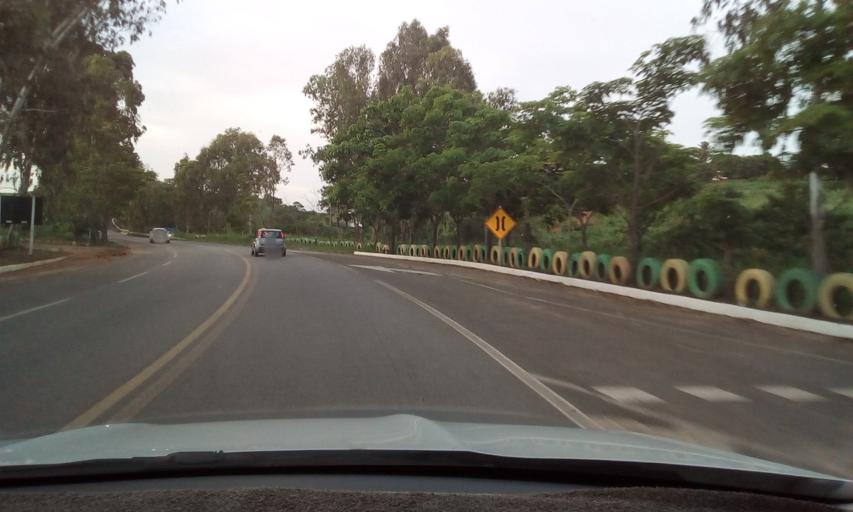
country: BR
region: Pernambuco
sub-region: Vicencia
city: Vicencia
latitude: -7.6157
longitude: -35.2392
